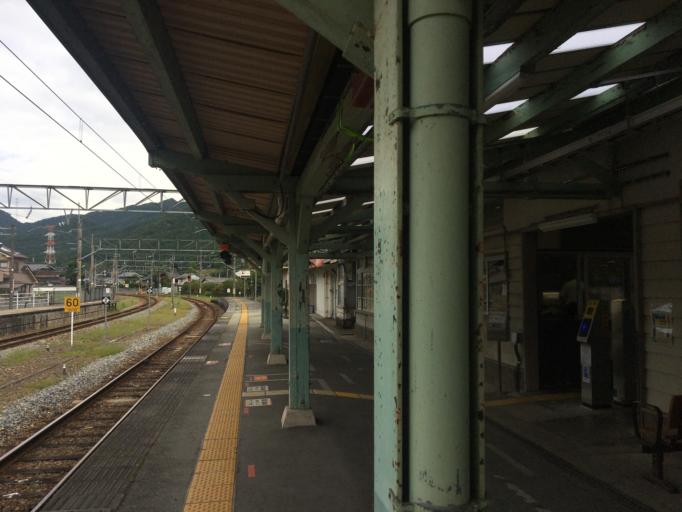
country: JP
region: Hyogo
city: Nishiwaki
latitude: 35.0825
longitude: 135.0501
